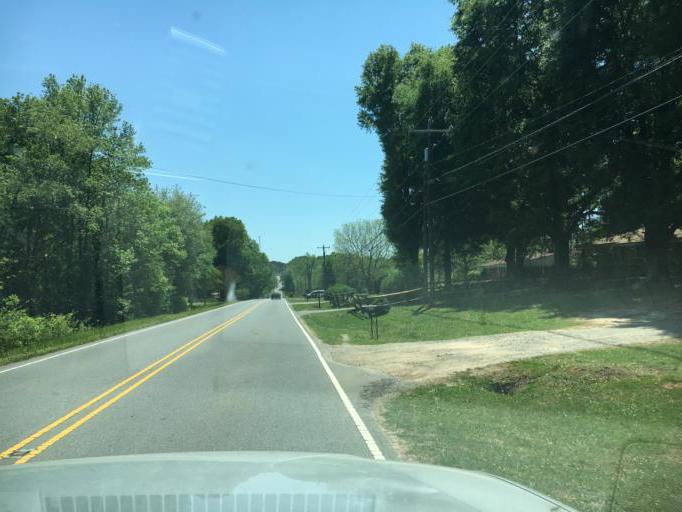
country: US
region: North Carolina
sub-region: Cleveland County
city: Shelby
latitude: 35.2196
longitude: -81.5651
